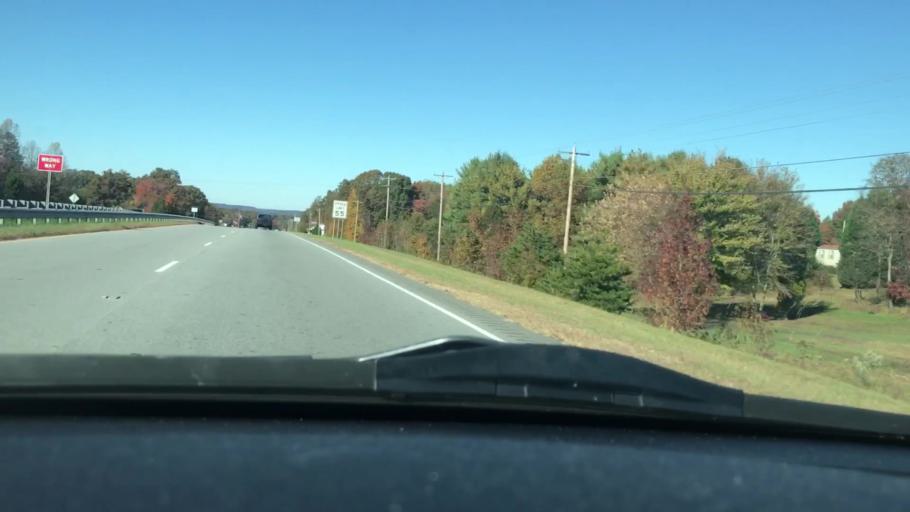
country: US
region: North Carolina
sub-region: Rockingham County
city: Madison
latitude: 36.3456
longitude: -79.9444
